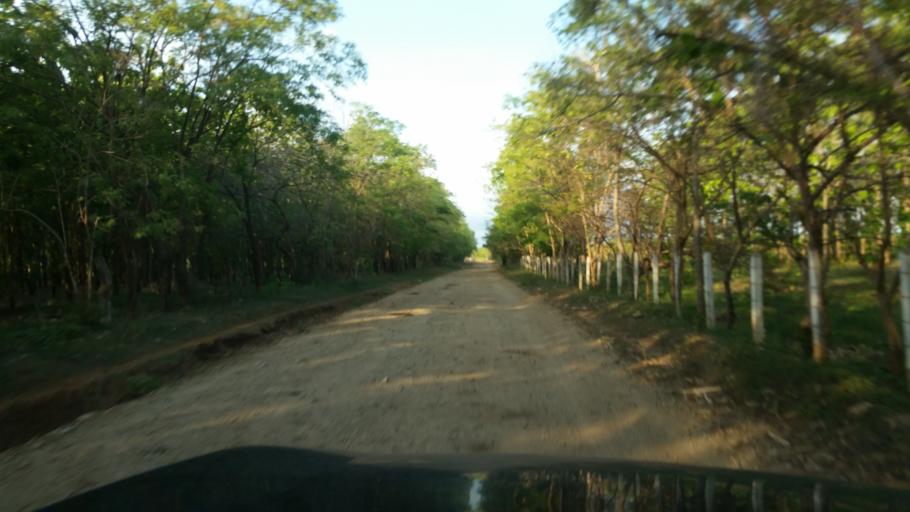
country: NI
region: Managua
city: Masachapa
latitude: 11.7746
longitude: -86.4866
